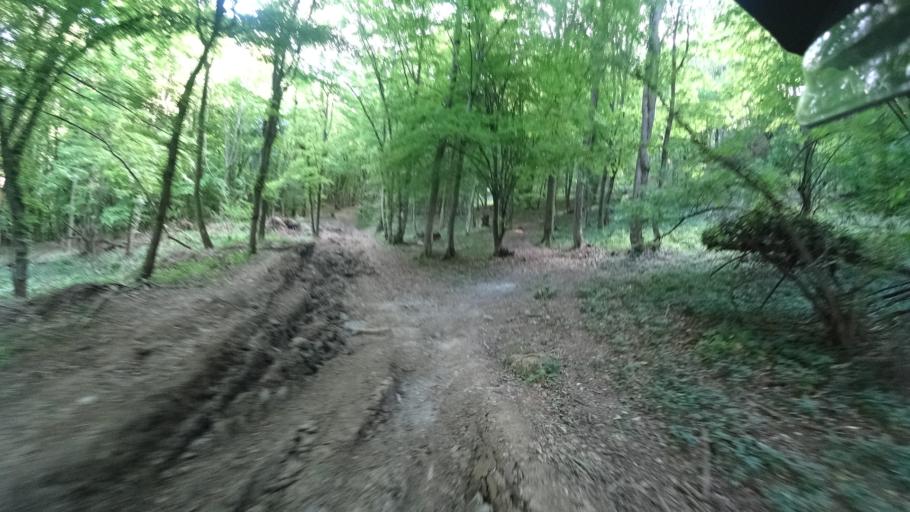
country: HR
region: Zagrebacka
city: Jablanovec
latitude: 45.8672
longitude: 15.8797
